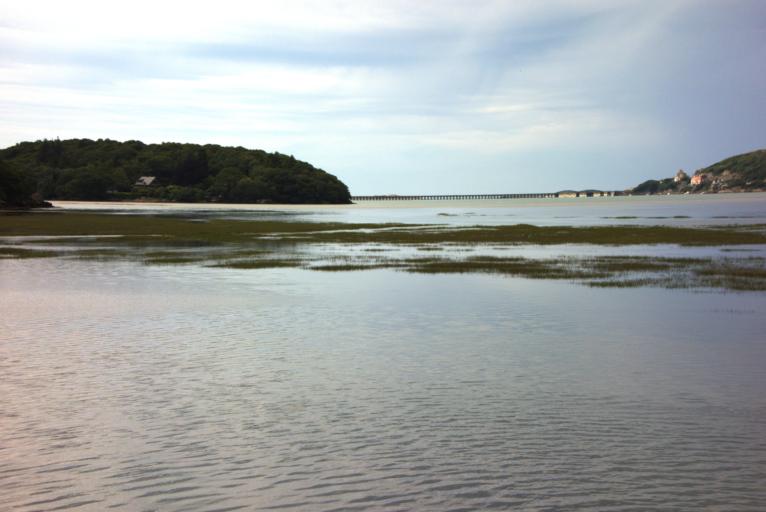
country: GB
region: Wales
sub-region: Gwynedd
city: Barmouth
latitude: 52.7238
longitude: -3.9992
